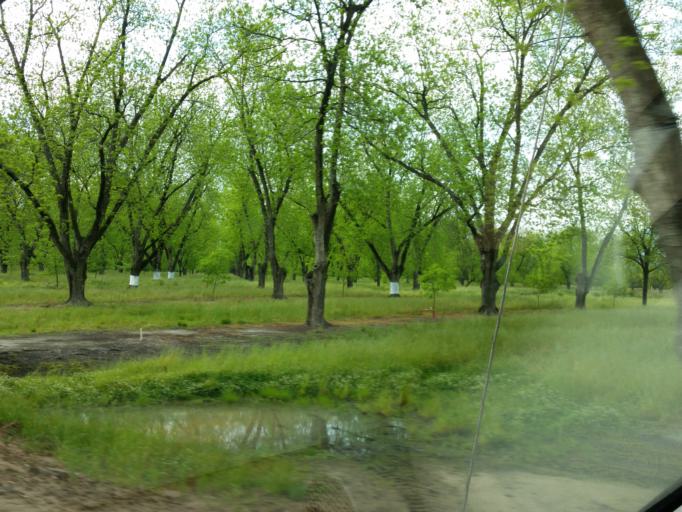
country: US
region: Georgia
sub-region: Dooly County
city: Vienna
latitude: 32.1579
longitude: -83.7614
